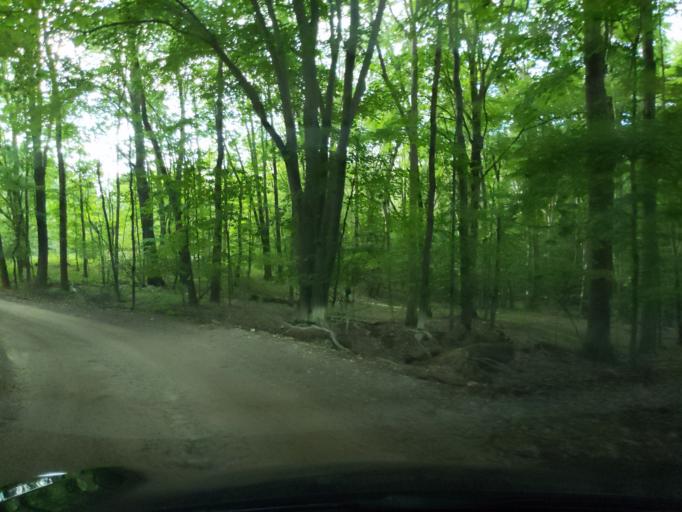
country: US
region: Michigan
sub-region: Eaton County
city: Dimondale
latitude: 42.5999
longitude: -84.5917
